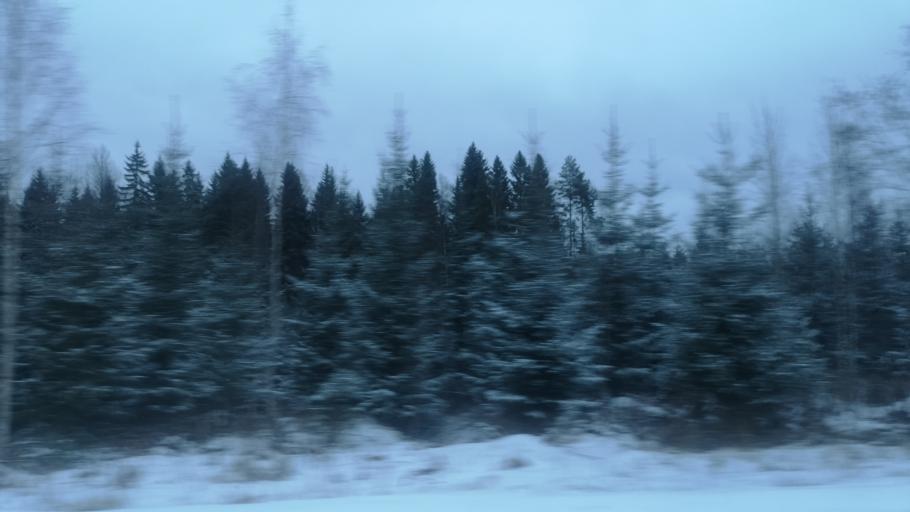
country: FI
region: Southern Savonia
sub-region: Savonlinna
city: Enonkoski
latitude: 62.0774
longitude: 28.7117
